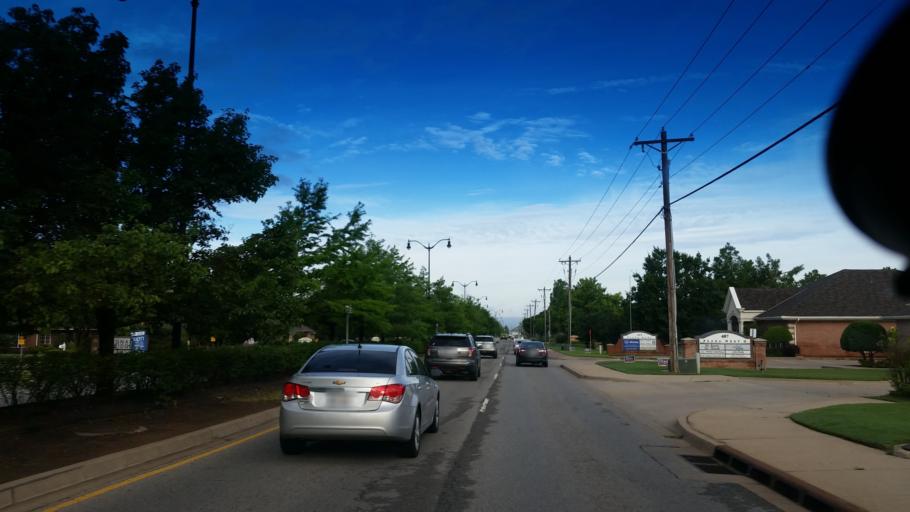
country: US
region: Oklahoma
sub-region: Oklahoma County
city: Edmond
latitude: 35.6384
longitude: -97.4896
